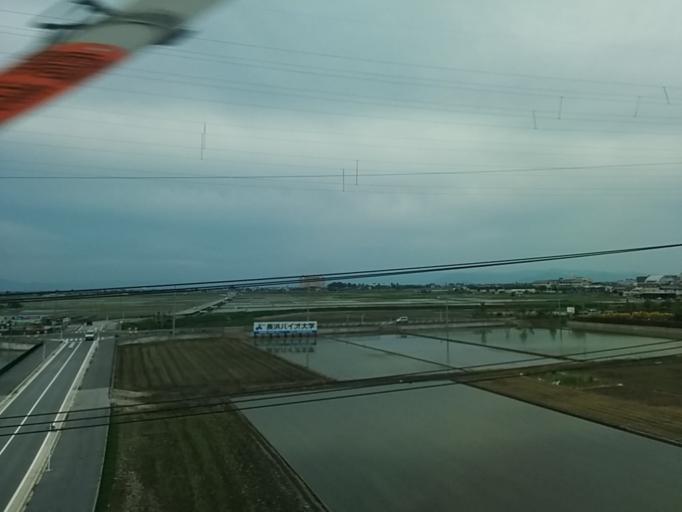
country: JP
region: Shiga Prefecture
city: Hikone
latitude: 35.3060
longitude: 136.2859
